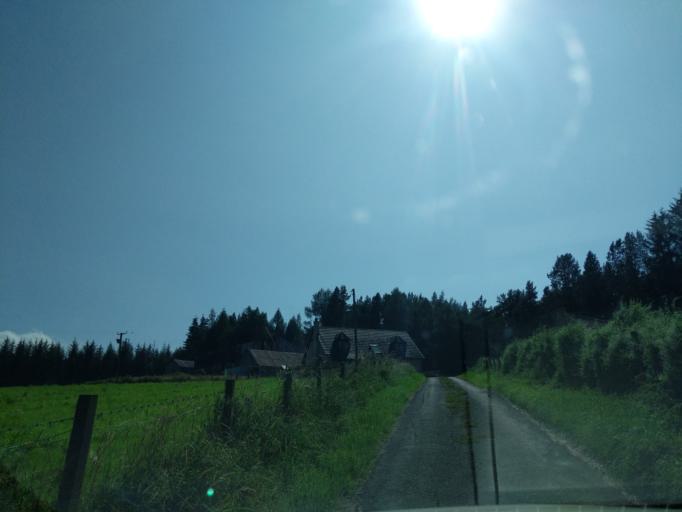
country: GB
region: Scotland
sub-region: Moray
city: Fochabers
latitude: 57.5886
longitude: -3.1109
